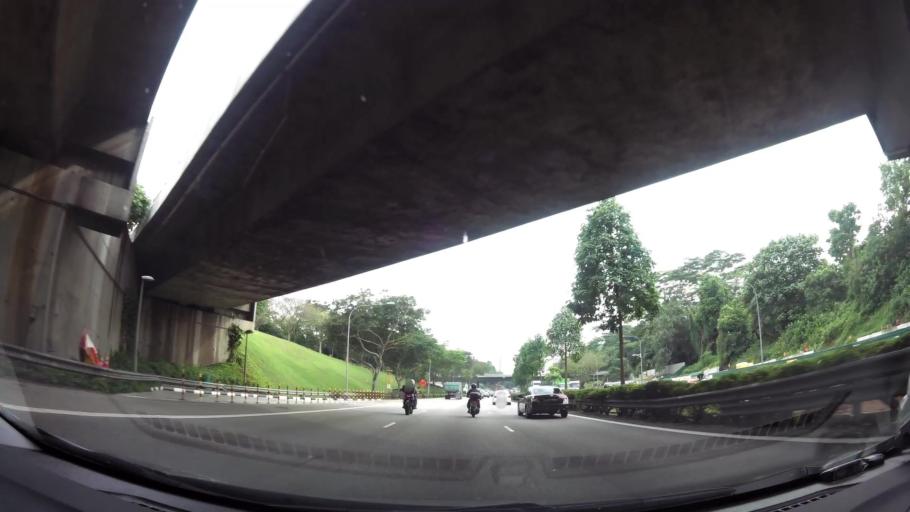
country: MY
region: Johor
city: Johor Bahru
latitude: 1.4142
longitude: 103.8058
